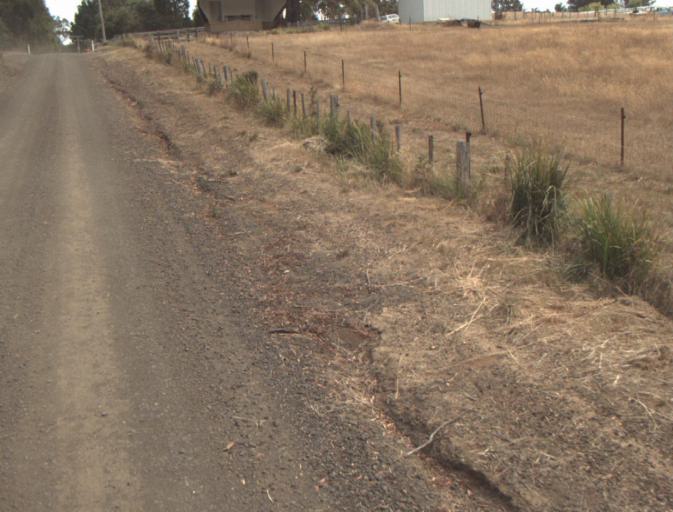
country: AU
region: Tasmania
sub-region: Launceston
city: Mayfield
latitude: -41.2789
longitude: 147.0450
